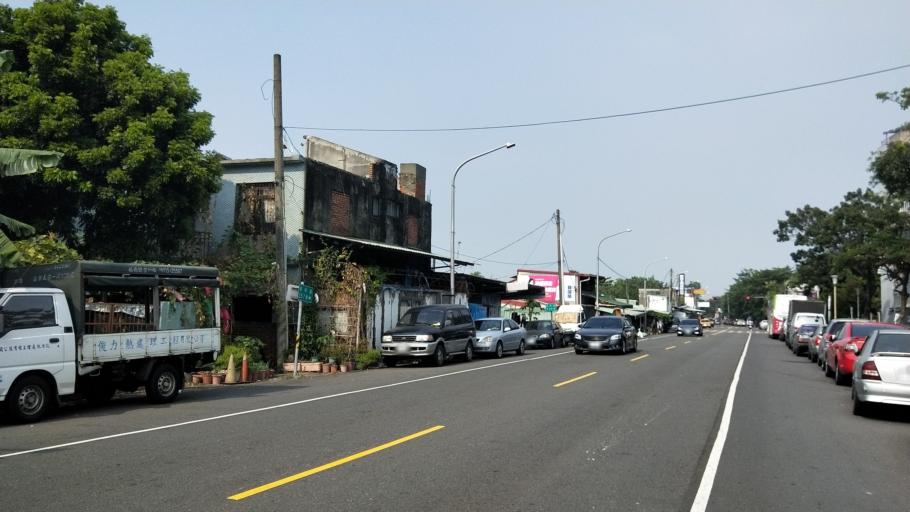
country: TW
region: Kaohsiung
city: Kaohsiung
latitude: 22.6751
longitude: 120.2910
